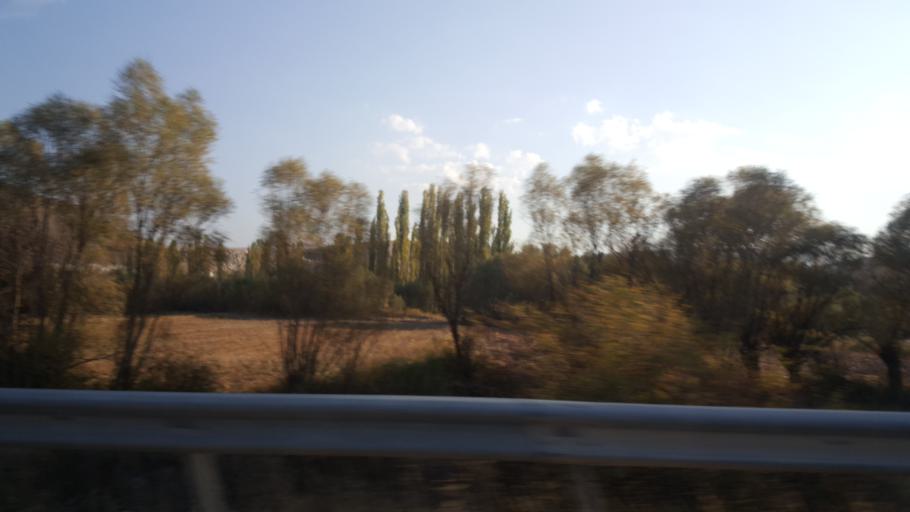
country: TR
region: Eskisehir
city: Seyitgazi
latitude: 39.4152
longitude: 30.6425
